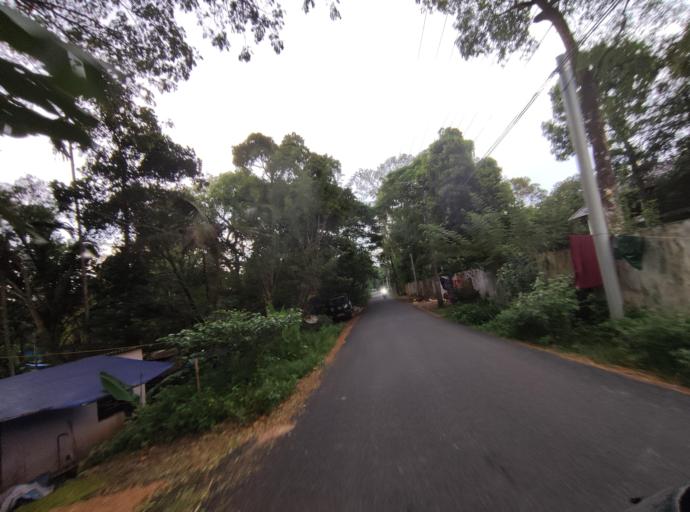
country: IN
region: Kerala
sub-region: Alappuzha
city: Shertallai
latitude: 9.6705
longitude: 76.3335
